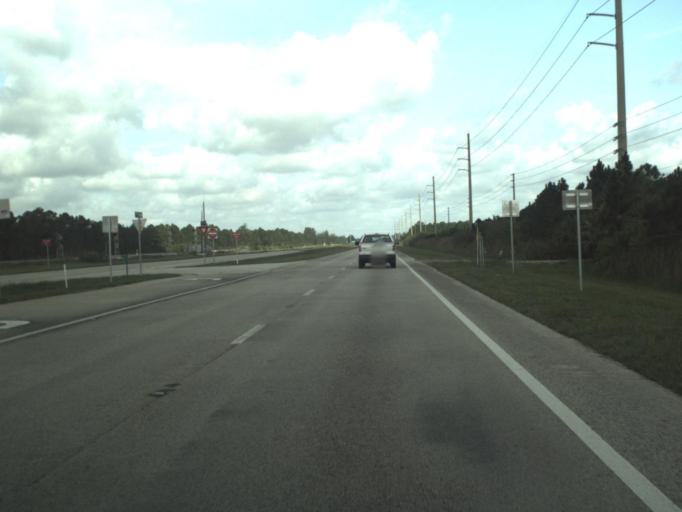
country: US
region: Florida
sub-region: Palm Beach County
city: Palm Beach Gardens
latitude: 26.8569
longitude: -80.2224
